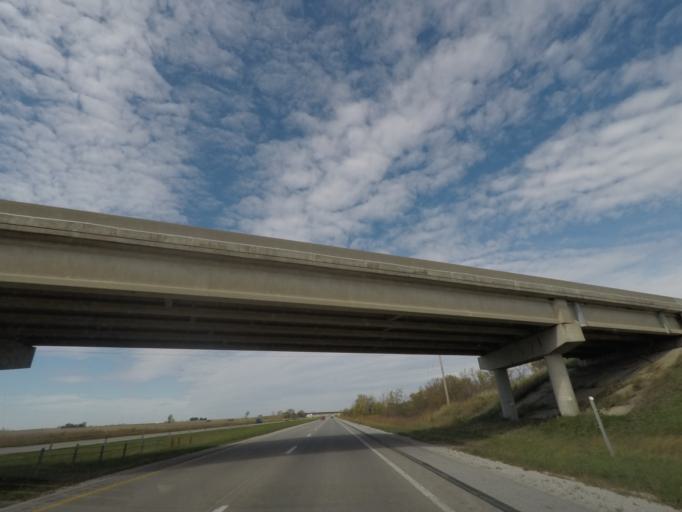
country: US
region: Iowa
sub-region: Story County
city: Ames
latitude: 42.0204
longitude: -93.7181
